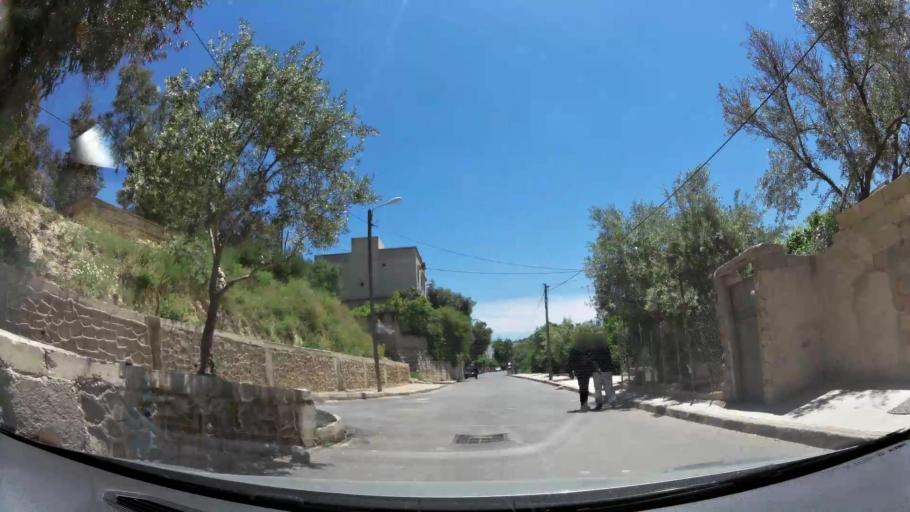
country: MA
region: Meknes-Tafilalet
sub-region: Meknes
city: Meknes
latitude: 33.9072
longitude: -5.5646
